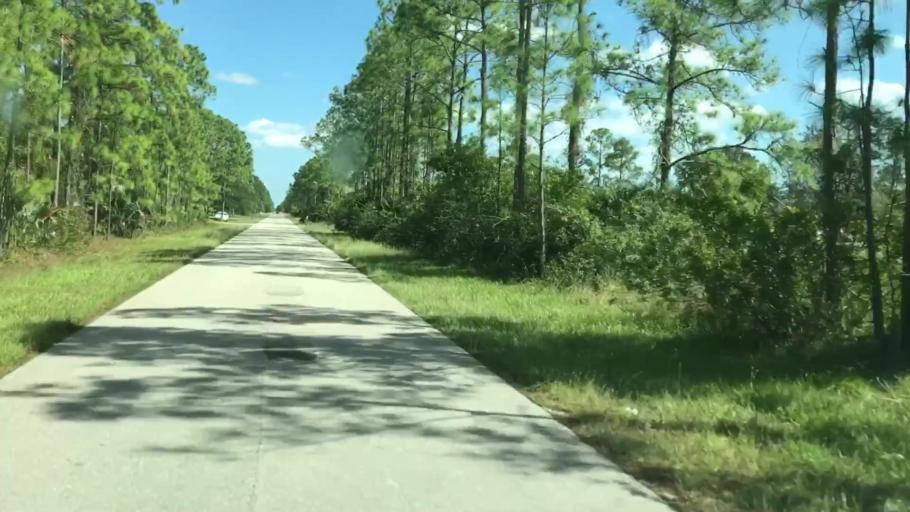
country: US
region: Florida
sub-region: Lee County
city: Lehigh Acres
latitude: 26.6283
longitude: -81.6433
